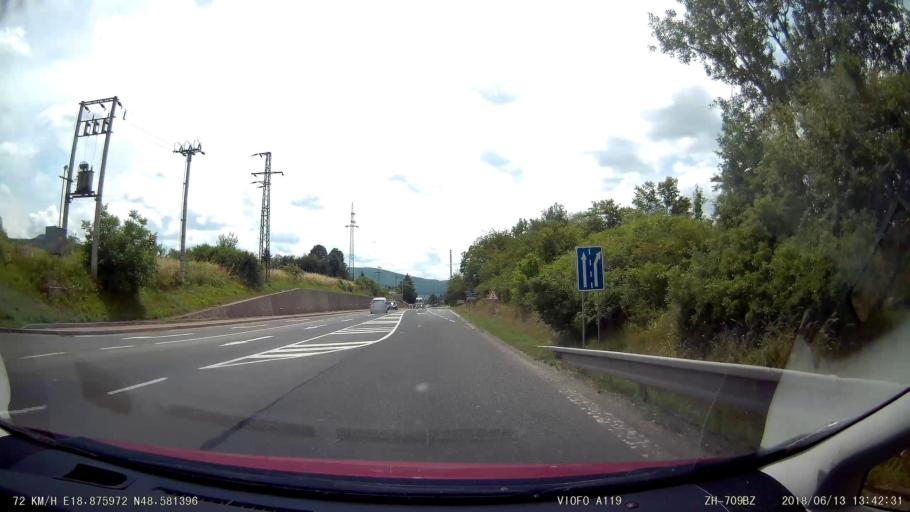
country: SK
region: Banskobystricky
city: Ziar nad Hronom
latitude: 48.5811
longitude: 18.8756
